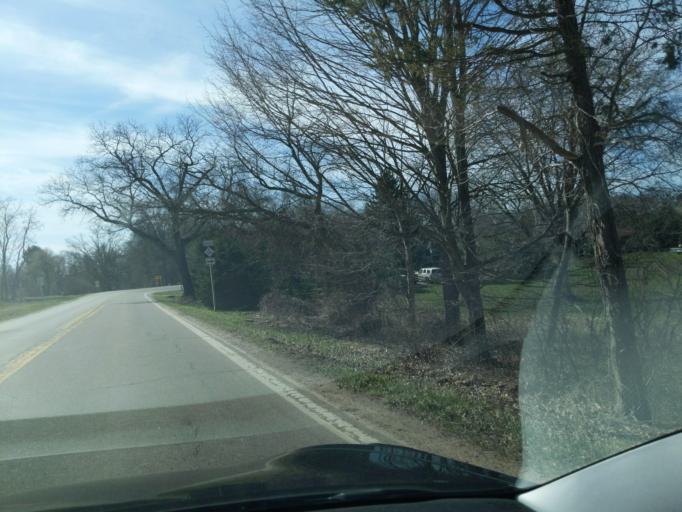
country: US
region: Michigan
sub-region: Ingham County
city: Stockbridge
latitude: 42.4463
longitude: -84.1114
